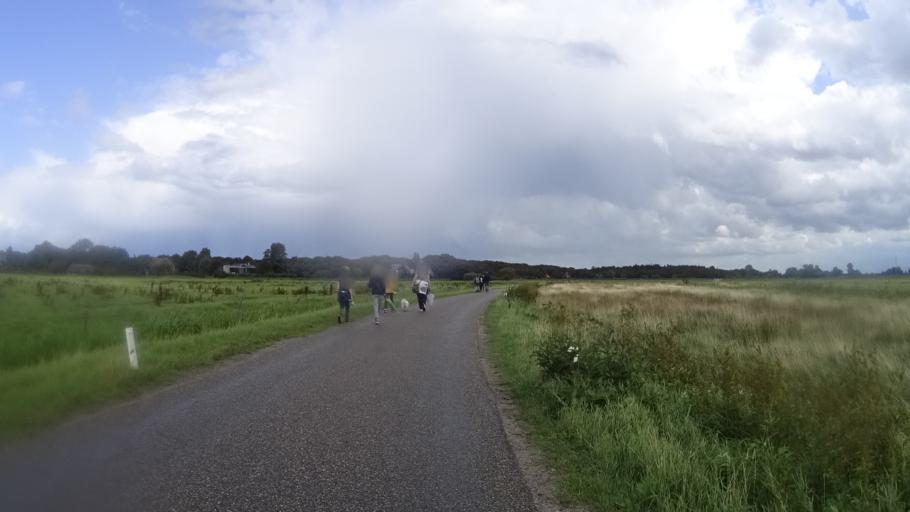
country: NL
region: North Holland
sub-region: Gemeente Heiloo
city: Heiloo
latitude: 52.6605
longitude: 4.6811
